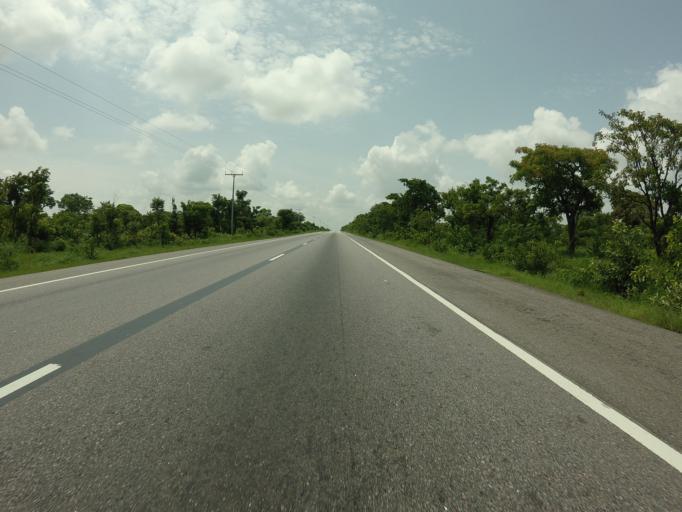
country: GH
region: Northern
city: Tamale
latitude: 9.1300
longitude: -1.2342
